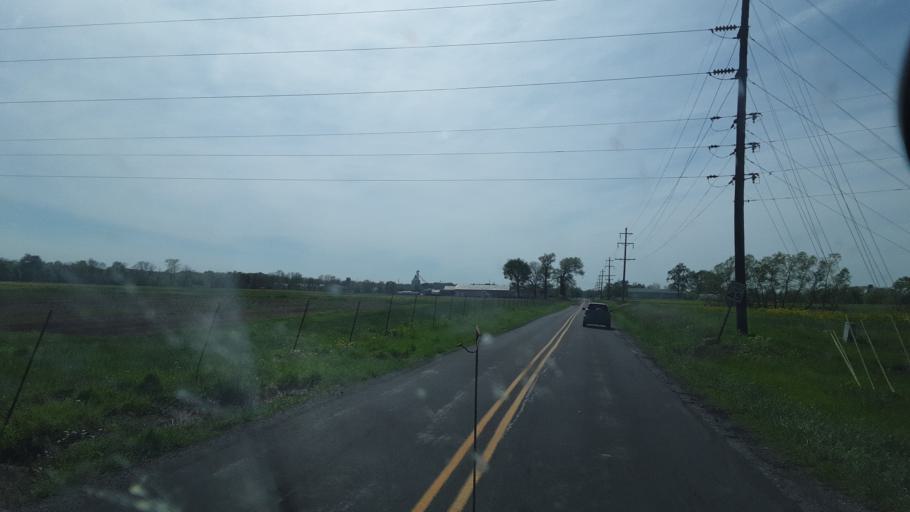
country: US
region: Illinois
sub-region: Jackson County
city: Carbondale
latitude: 37.7009
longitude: -89.2382
